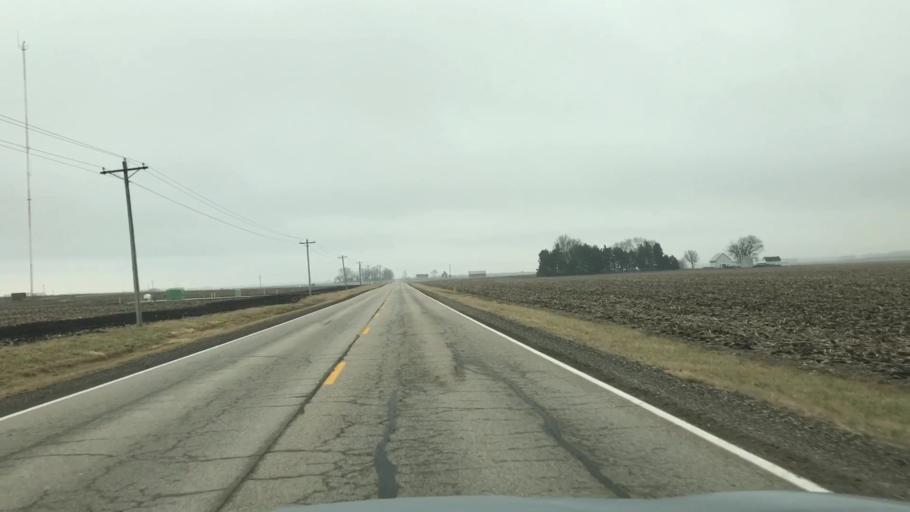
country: US
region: Illinois
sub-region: McLean County
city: Hudson
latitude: 40.5818
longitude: -88.9449
